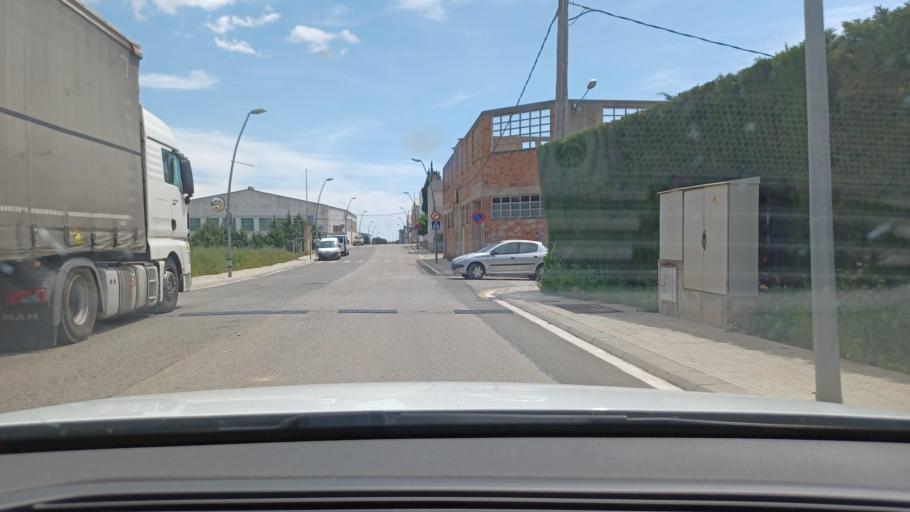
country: ES
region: Valencia
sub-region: Provincia de Castello
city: Rosell
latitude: 40.6348
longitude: 0.2872
